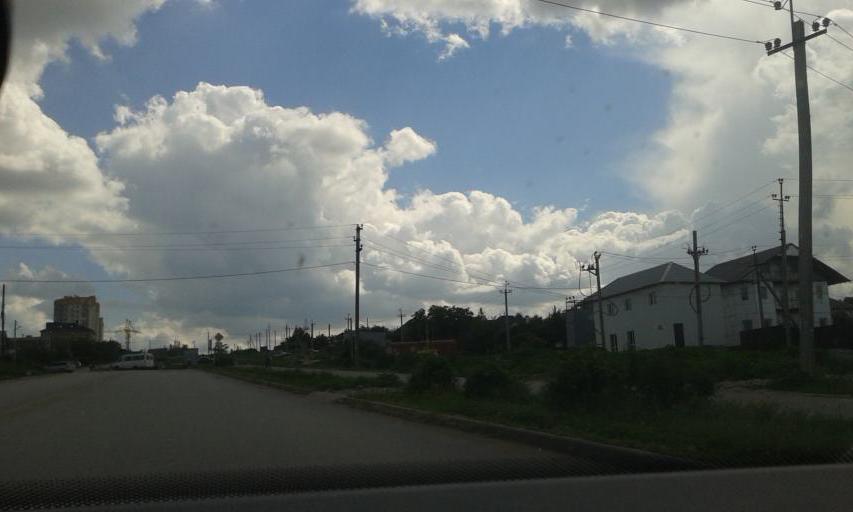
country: RU
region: Volgograd
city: Volgograd
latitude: 48.6514
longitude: 44.4121
